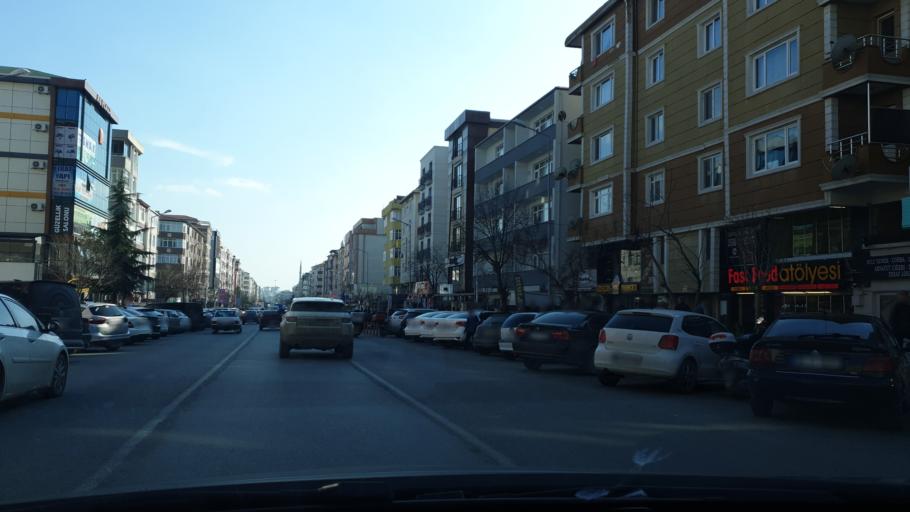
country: TR
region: Tekirdag
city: Cerkezkoey
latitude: 41.2938
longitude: 27.9979
